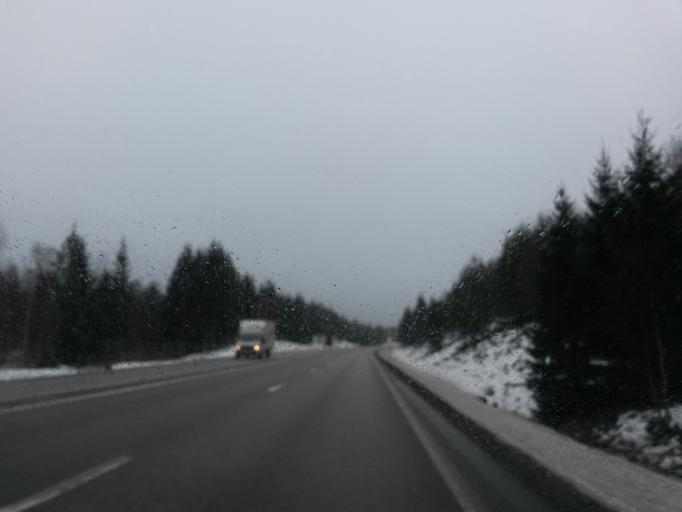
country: SE
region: Vaestra Goetaland
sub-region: Marks Kommun
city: Fritsla
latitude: 57.5342
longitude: 12.7953
